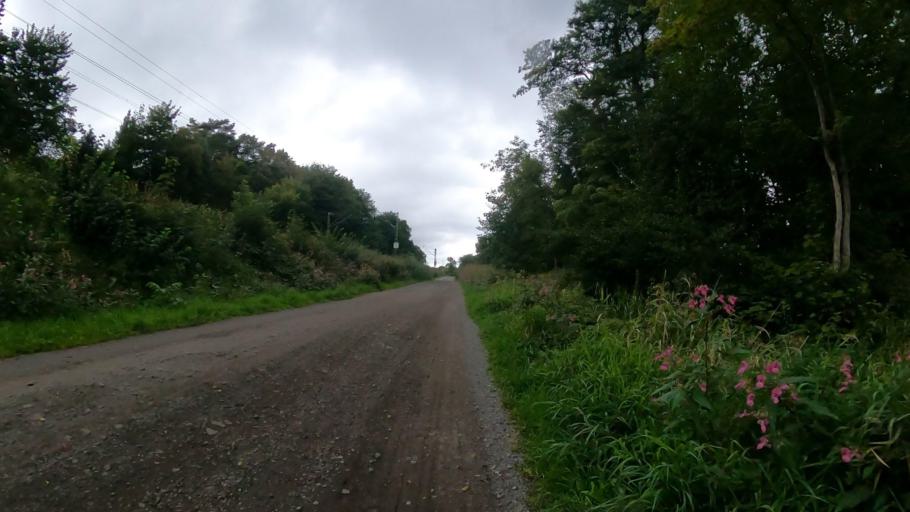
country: DE
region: Lower Saxony
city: Agathenburg
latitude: 53.5603
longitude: 9.5394
